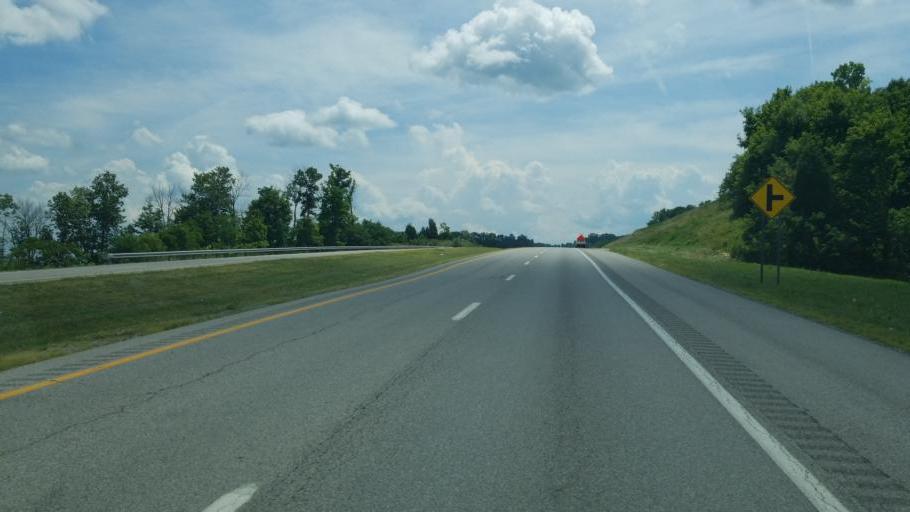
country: US
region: West Virginia
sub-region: Mason County
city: Point Pleasant
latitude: 38.8089
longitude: -82.1055
